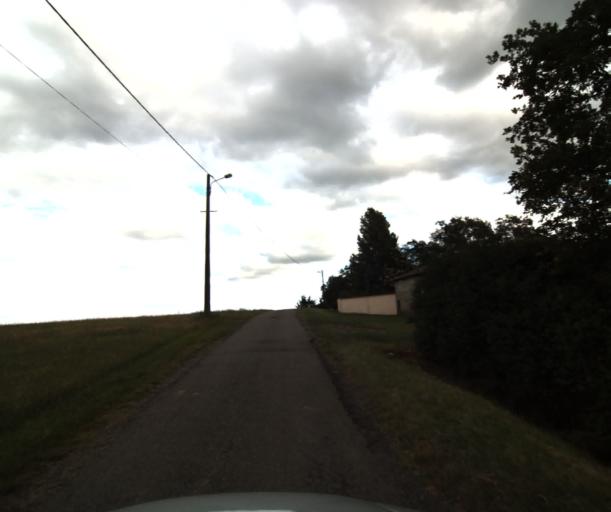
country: FR
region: Midi-Pyrenees
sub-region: Departement de la Haute-Garonne
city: Le Fauga
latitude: 43.4011
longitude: 1.3262
